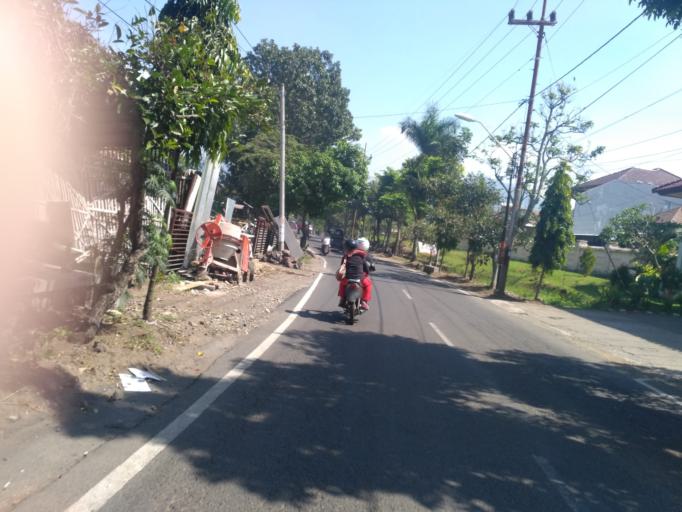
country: ID
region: East Java
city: Batu
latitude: -7.8635
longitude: 112.5343
